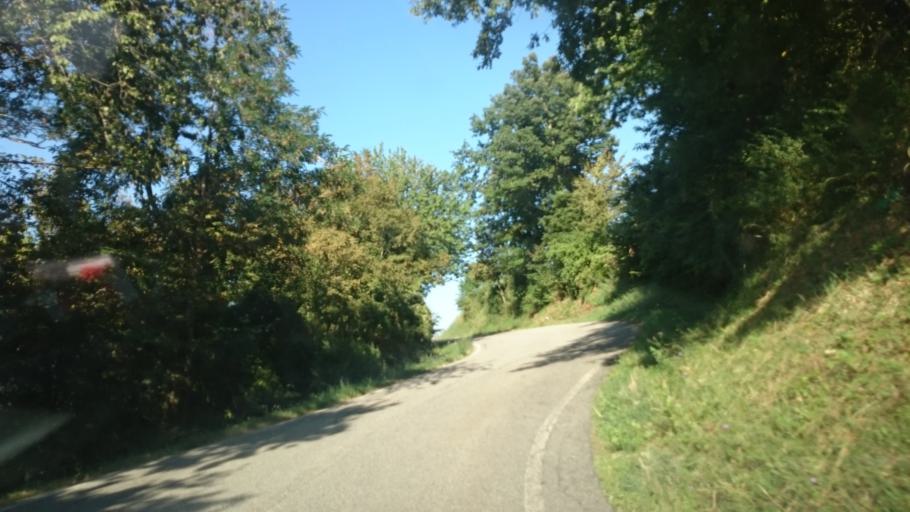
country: IT
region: Emilia-Romagna
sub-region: Provincia di Reggio Emilia
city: Villa Minozzo
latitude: 44.3486
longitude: 10.4870
